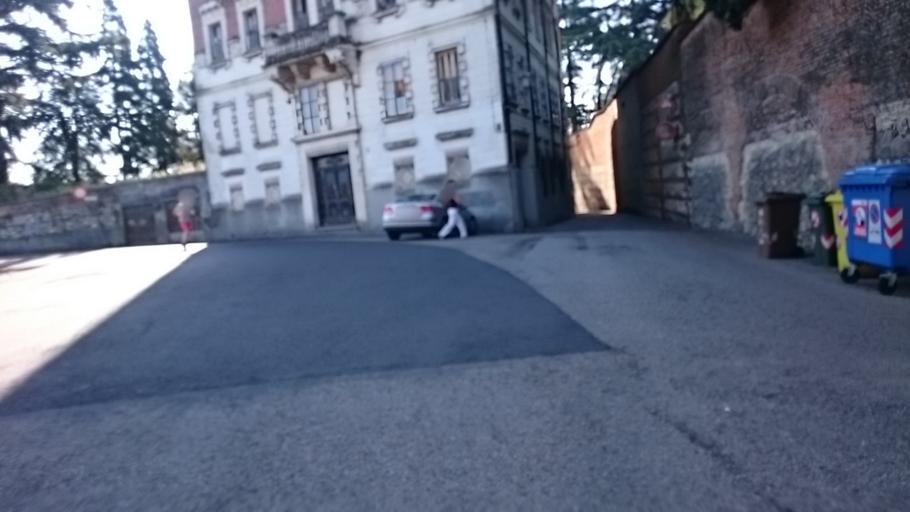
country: IT
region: Veneto
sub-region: Provincia di Vicenza
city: Vicenza
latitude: 45.5382
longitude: 11.5512
